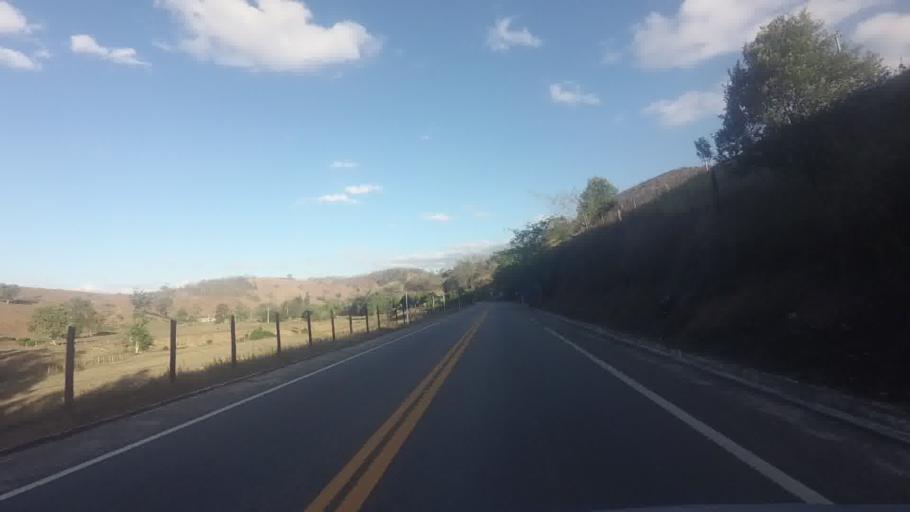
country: BR
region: Espirito Santo
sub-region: Cachoeiro De Itapemirim
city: Cachoeiro de Itapemirim
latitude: -20.8254
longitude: -41.2159
